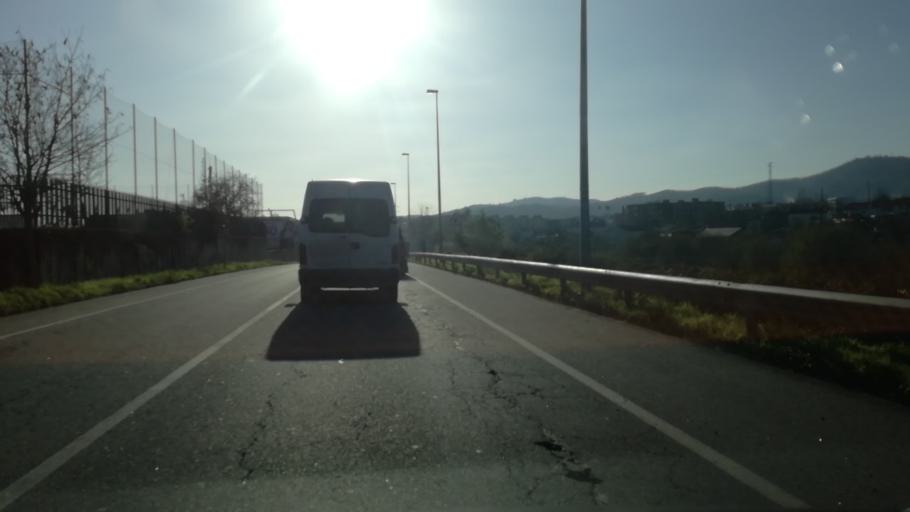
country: PT
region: Braga
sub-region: Guimaraes
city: Ponte
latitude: 41.4911
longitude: -8.3419
